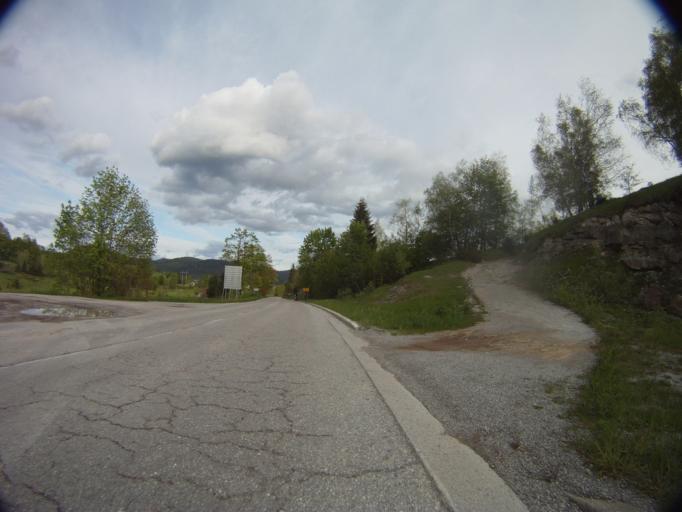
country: HR
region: Primorsko-Goranska
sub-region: Grad Delnice
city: Delnice
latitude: 45.3802
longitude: 14.9138
